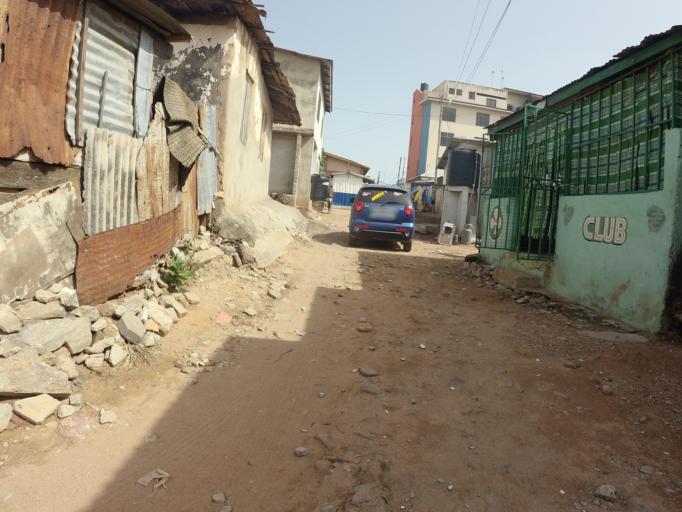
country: GH
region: Greater Accra
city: Dome
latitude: 5.6112
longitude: -0.2348
